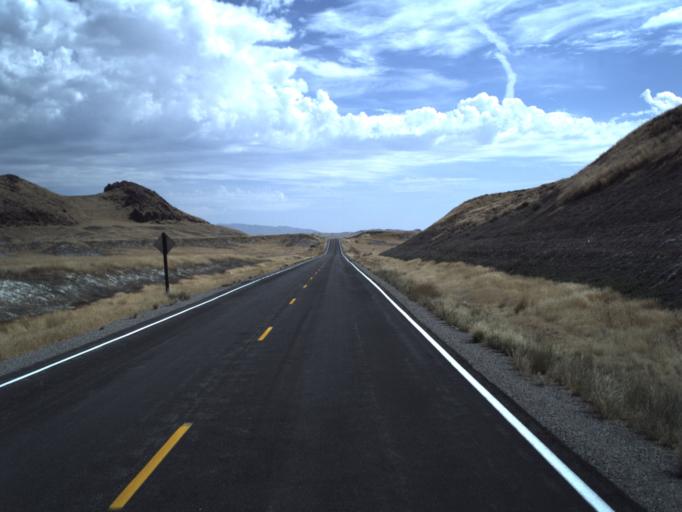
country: US
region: Utah
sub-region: Tooele County
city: Wendover
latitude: 41.3738
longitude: -114.0192
